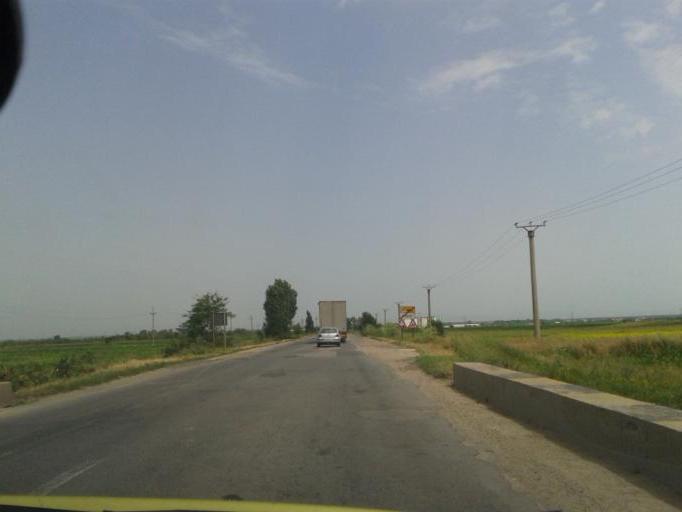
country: RO
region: Dambovita
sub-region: Oras Gaesti
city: Gaesti
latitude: 44.6879
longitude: 25.3135
